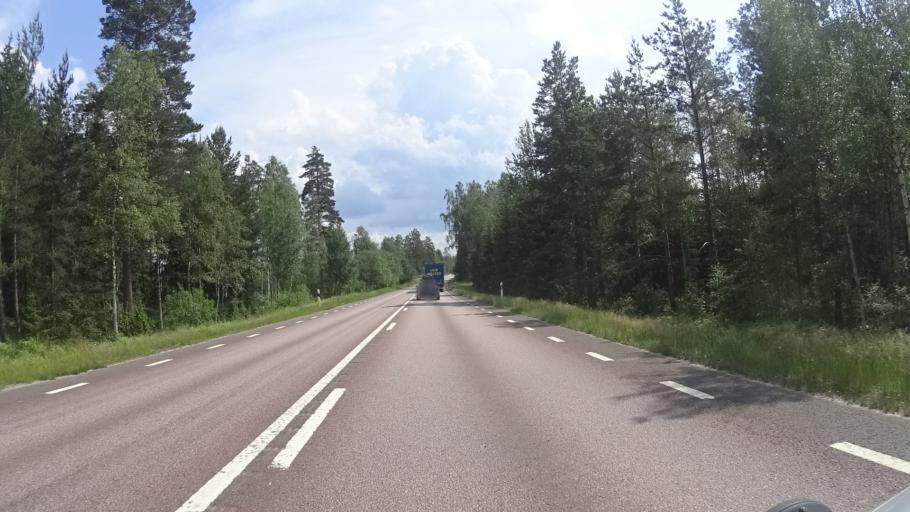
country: SE
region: Kalmar
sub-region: Hultsfreds Kommun
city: Hultsfred
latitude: 57.4769
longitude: 15.8369
